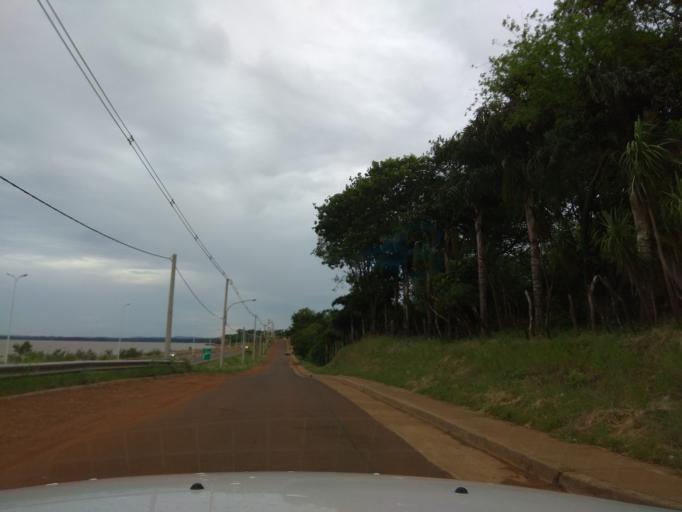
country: AR
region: Misiones
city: Garupa
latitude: -27.4397
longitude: -55.8543
